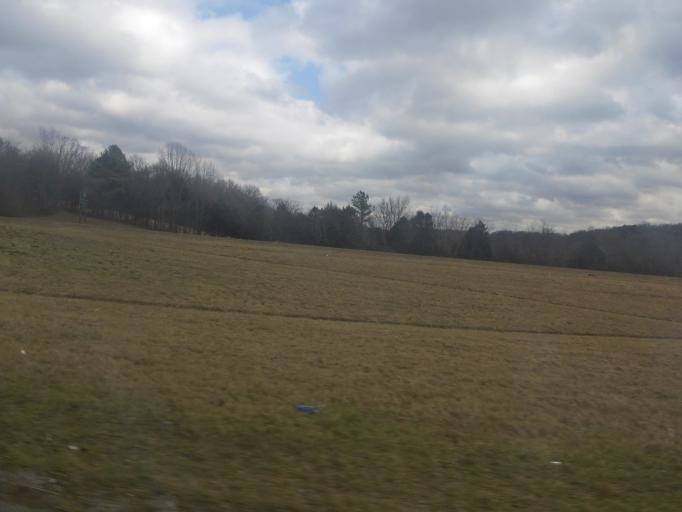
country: US
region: Tennessee
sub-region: Rutherford County
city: Plainview
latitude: 35.6093
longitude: -86.2405
